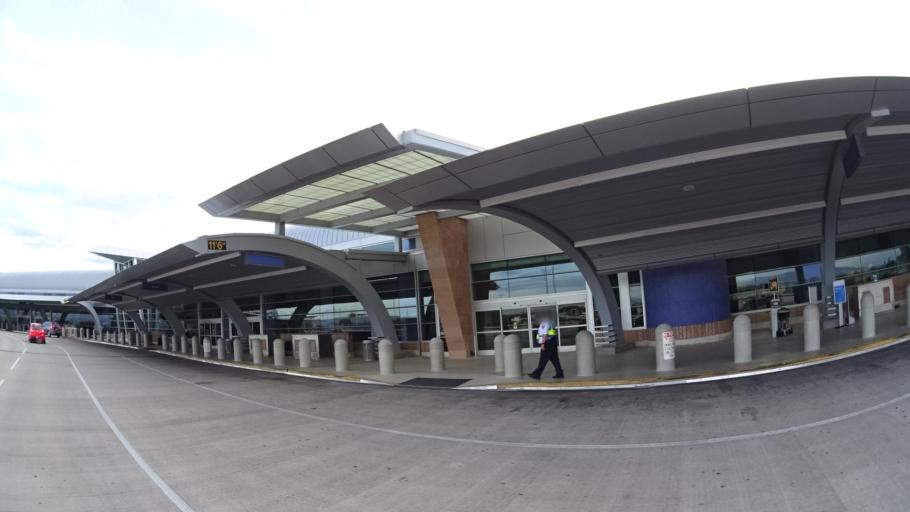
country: US
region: Arizona
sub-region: Pima County
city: Summit
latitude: 32.1209
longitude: -110.9375
